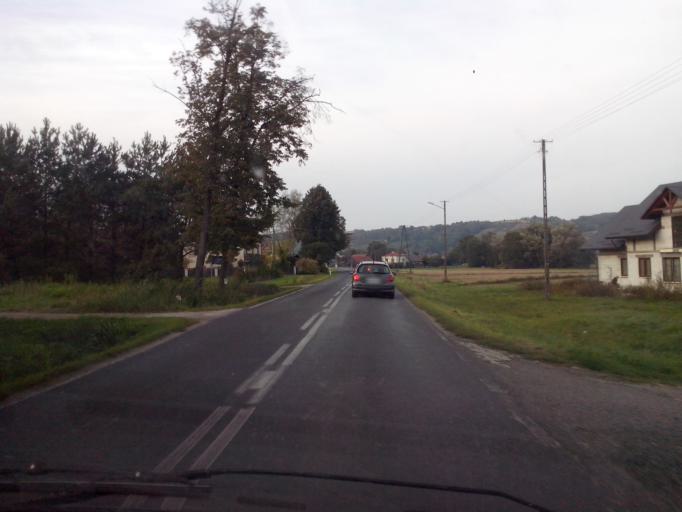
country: PL
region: Subcarpathian Voivodeship
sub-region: Powiat strzyzowski
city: Strzyzow
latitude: 49.8302
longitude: 21.8269
